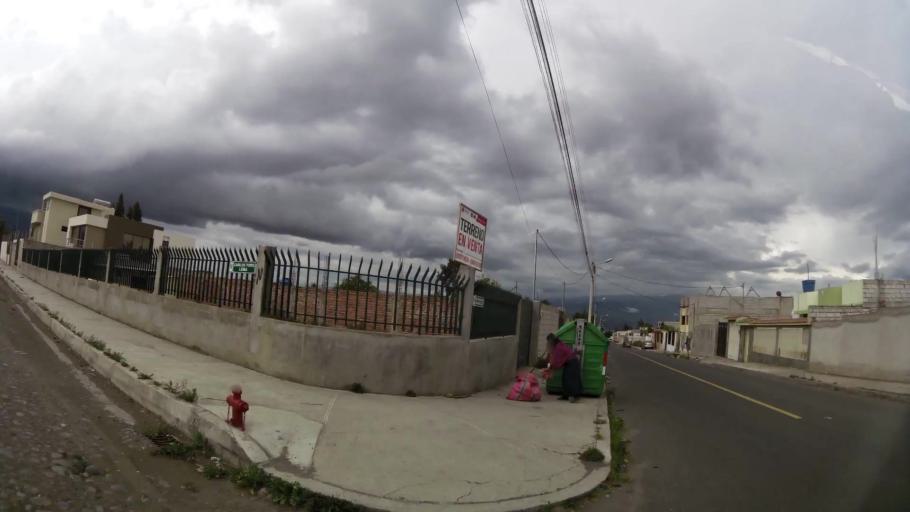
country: EC
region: Tungurahua
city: Ambato
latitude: -1.2807
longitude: -78.6219
